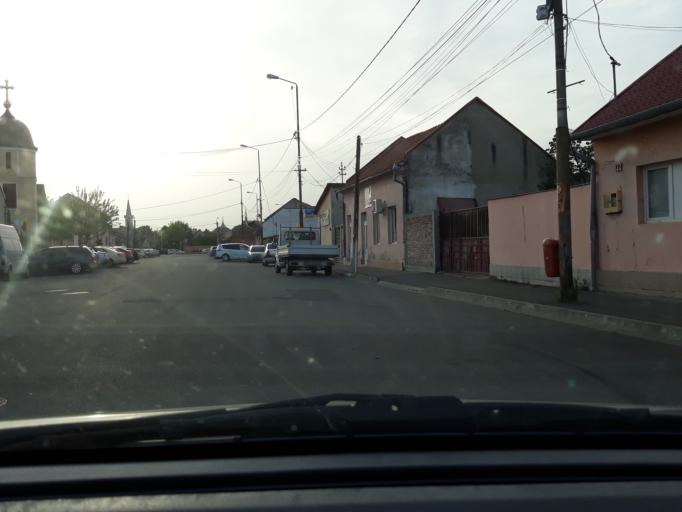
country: RO
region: Bihor
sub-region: Comuna Biharea
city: Oradea
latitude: 47.0474
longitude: 21.9596
